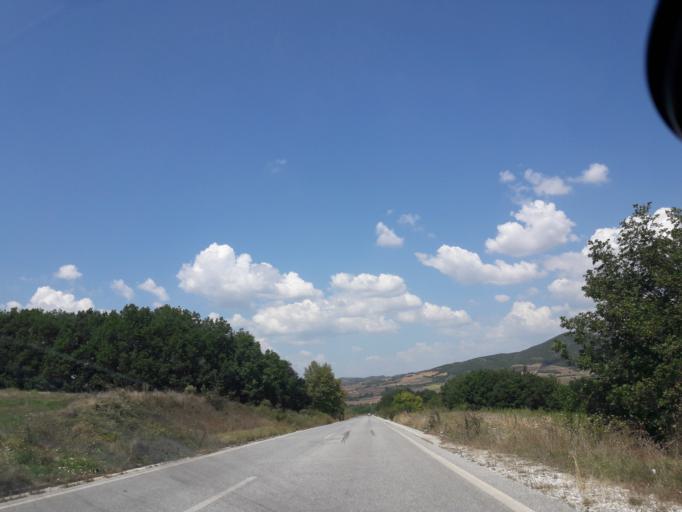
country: GR
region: Central Macedonia
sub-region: Nomos Chalkidikis
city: Polygyros
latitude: 40.4580
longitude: 23.4028
